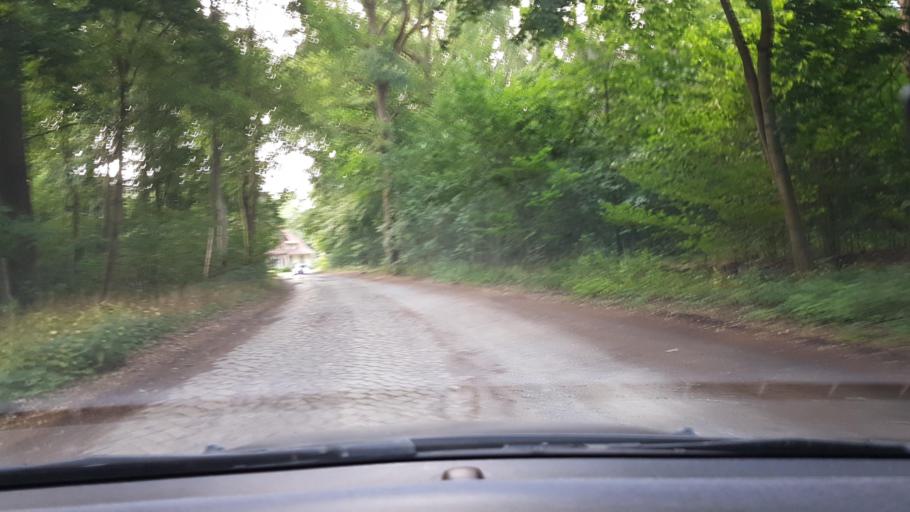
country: DE
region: Lower Saxony
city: Fassberg
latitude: 52.8717
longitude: 10.2272
